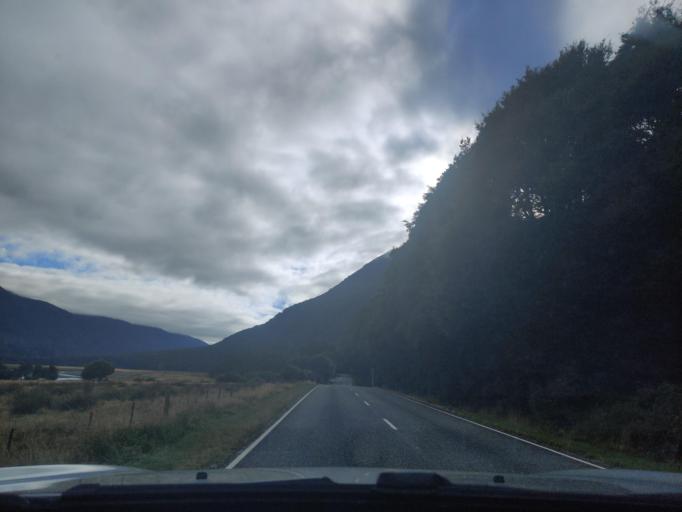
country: NZ
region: Otago
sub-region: Queenstown-Lakes District
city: Wanaka
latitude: -44.1921
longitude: 169.2549
